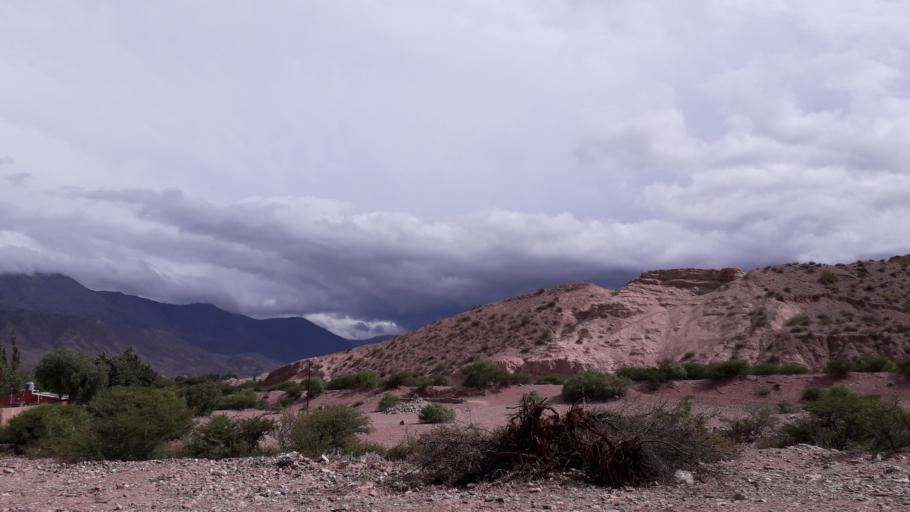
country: AR
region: Jujuy
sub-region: Departamento de Humahuaca
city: Humahuaca
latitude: -23.3052
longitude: -65.3592
